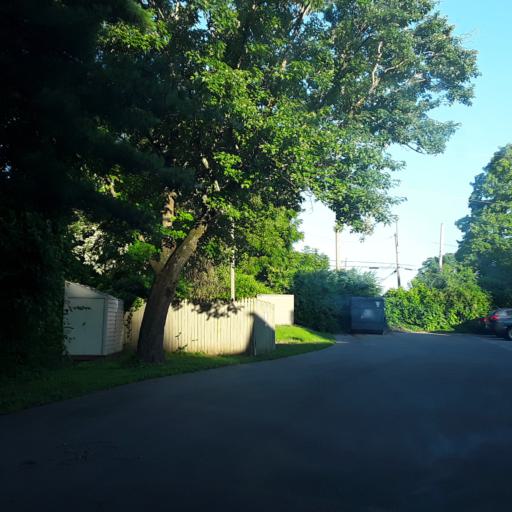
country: US
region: Tennessee
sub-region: Davidson County
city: Oak Hill
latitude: 36.1048
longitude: -86.7326
